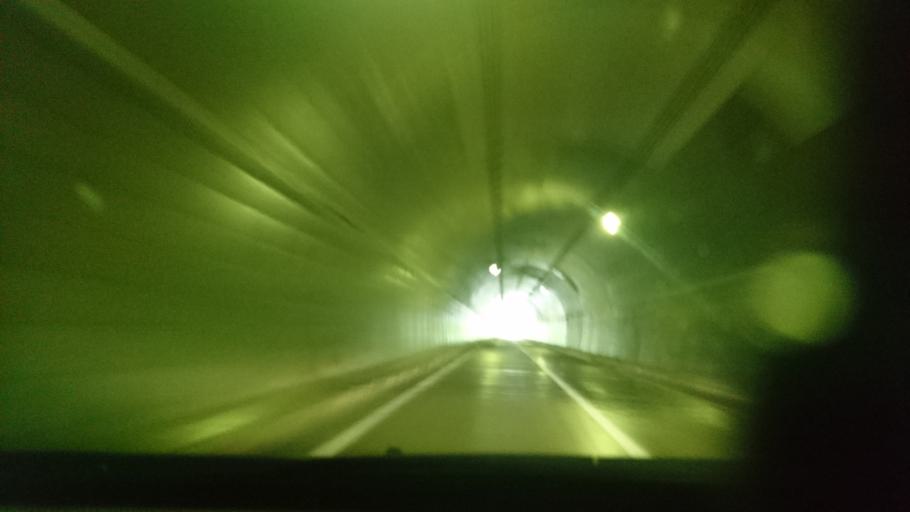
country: JP
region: Akita
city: Yuzawa
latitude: 39.1508
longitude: 140.7620
